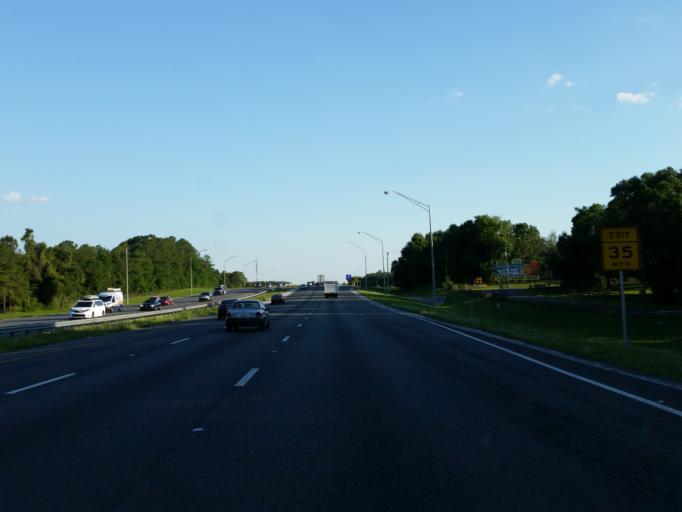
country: US
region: Florida
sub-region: Marion County
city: Ocala
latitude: 29.1004
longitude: -82.1851
